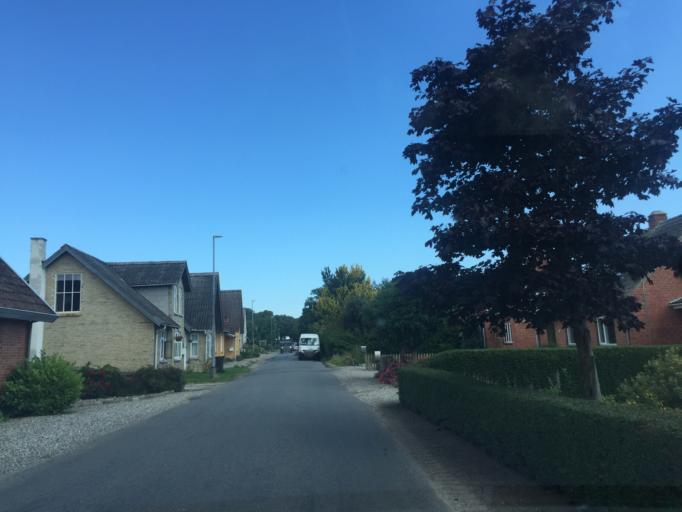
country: DK
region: South Denmark
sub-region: Nordfyns Kommune
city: Otterup
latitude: 55.5714
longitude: 10.3678
